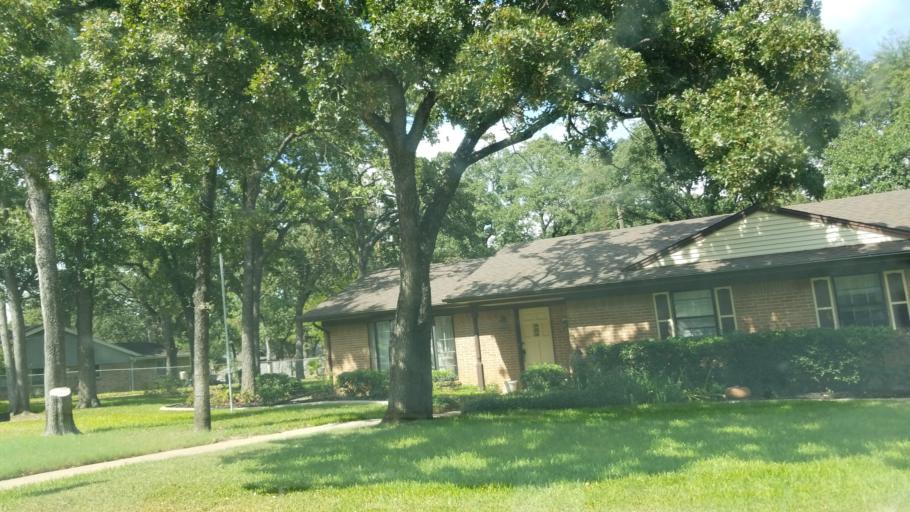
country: US
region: Texas
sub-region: Tarrant County
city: Euless
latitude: 32.8650
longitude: -97.0865
